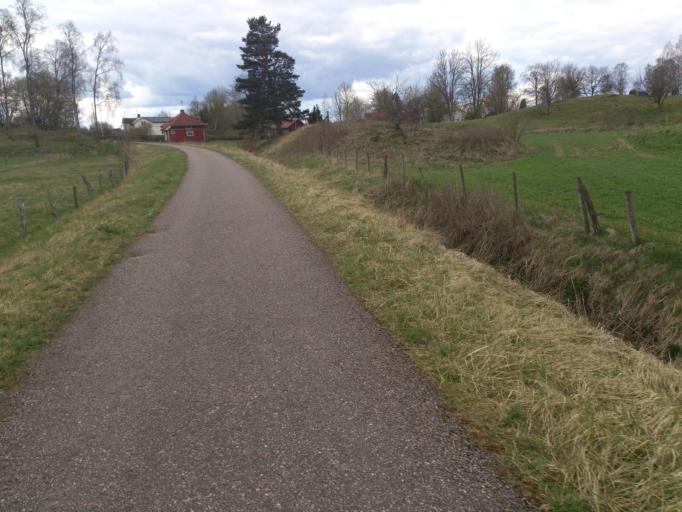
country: SE
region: Vaestra Goetaland
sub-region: Falkopings Kommun
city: Falkoeping
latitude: 57.9827
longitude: 13.5254
